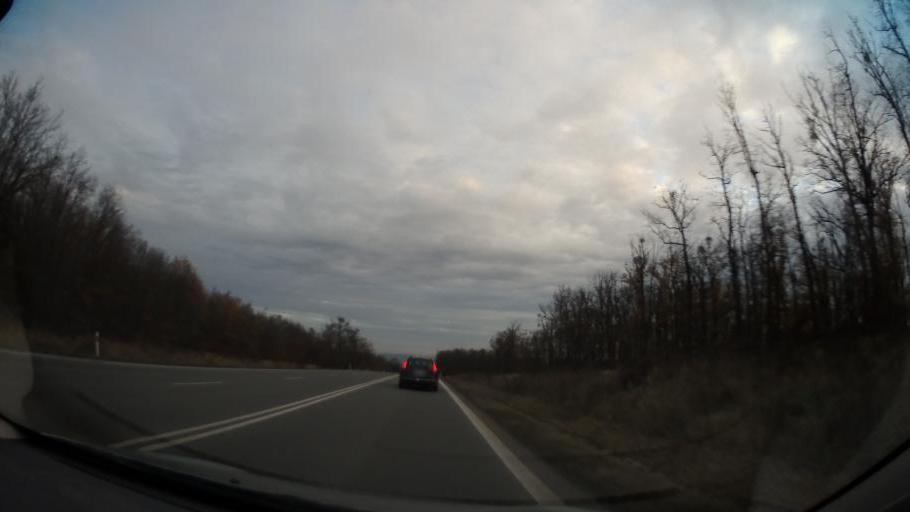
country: CZ
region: South Moravian
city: Troubsko
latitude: 49.1885
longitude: 16.4633
